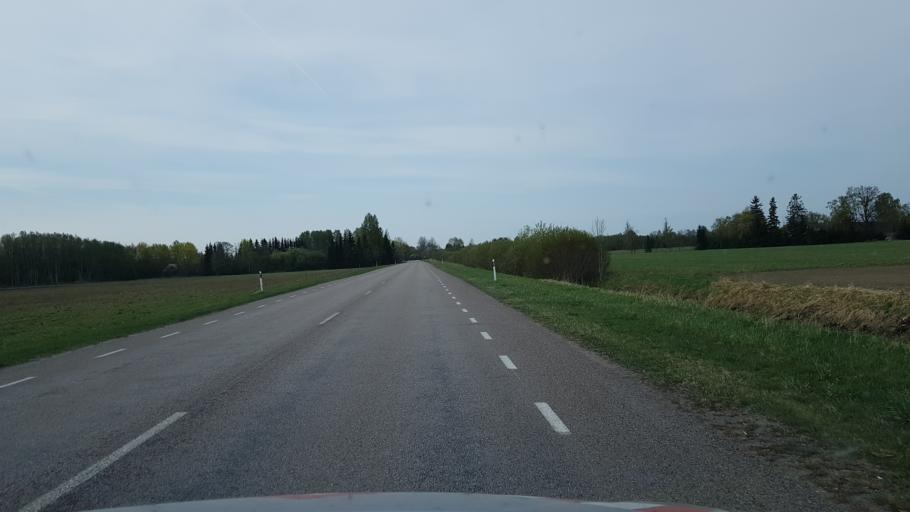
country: EE
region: Paernumaa
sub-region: Audru vald
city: Audru
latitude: 58.3763
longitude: 24.2704
